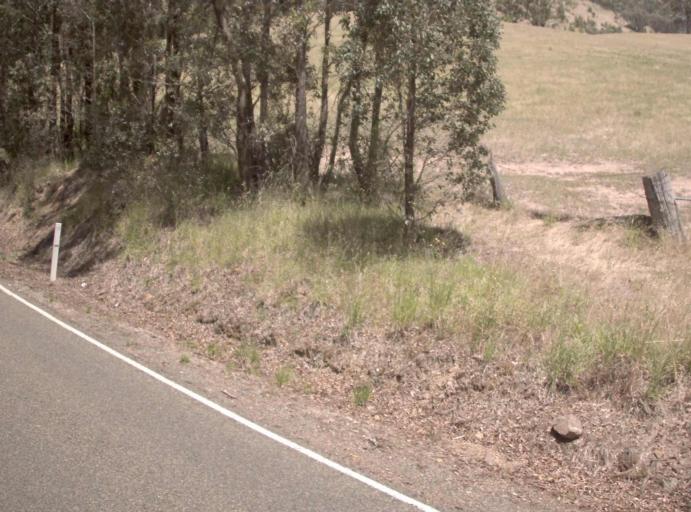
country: AU
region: Victoria
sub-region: East Gippsland
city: Bairnsdale
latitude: -37.4147
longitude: 147.8334
